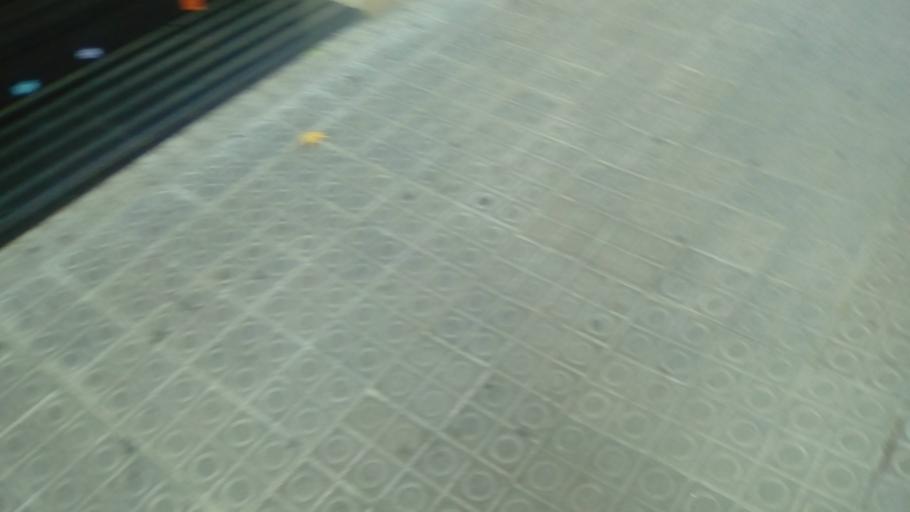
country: ES
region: Catalonia
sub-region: Provincia de Barcelona
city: Manresa
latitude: 41.7278
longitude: 1.8244
